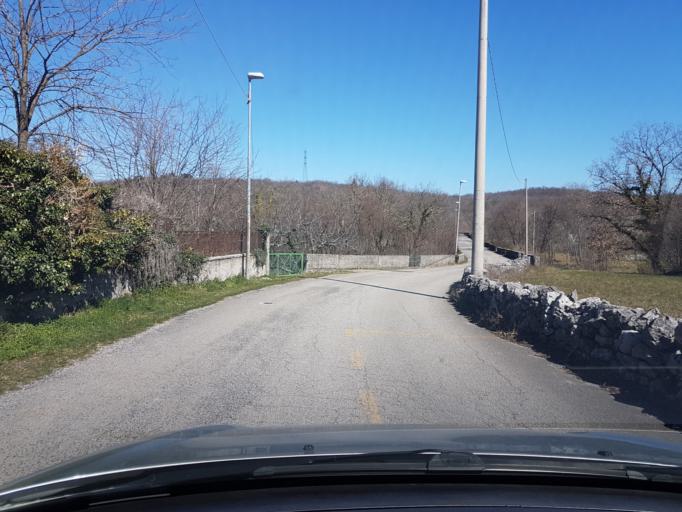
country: IT
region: Friuli Venezia Giulia
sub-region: Provincia di Trieste
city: Sistiana-Visogliano
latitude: 45.7854
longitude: 13.6435
